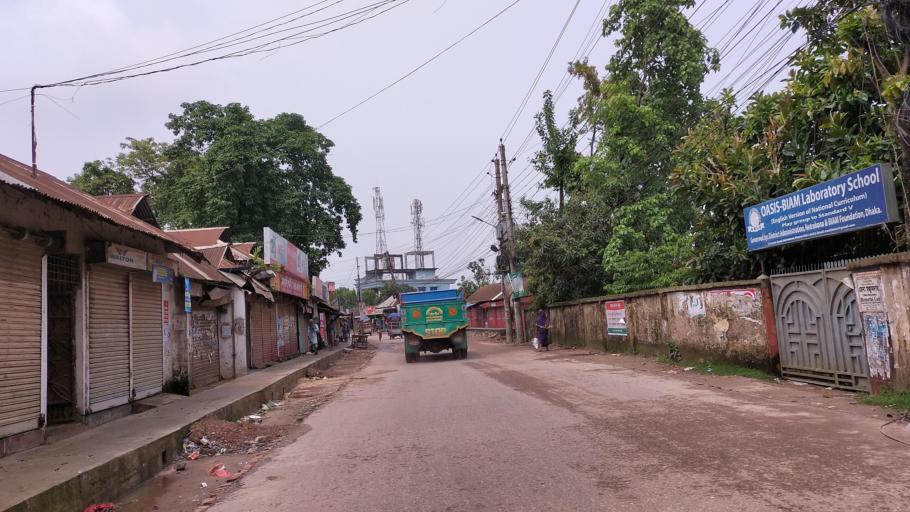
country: BD
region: Dhaka
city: Netrakona
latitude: 24.8873
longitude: 90.7374
